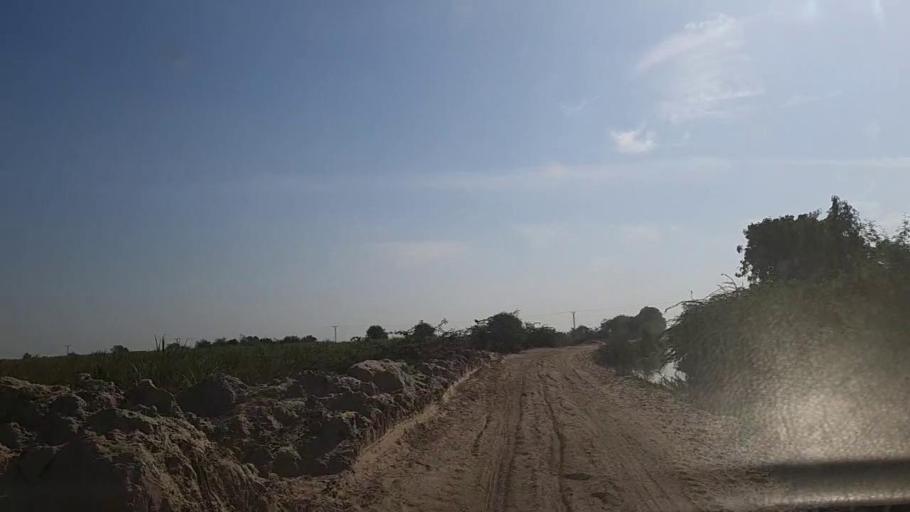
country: PK
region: Sindh
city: Bulri
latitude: 24.8373
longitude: 68.2814
